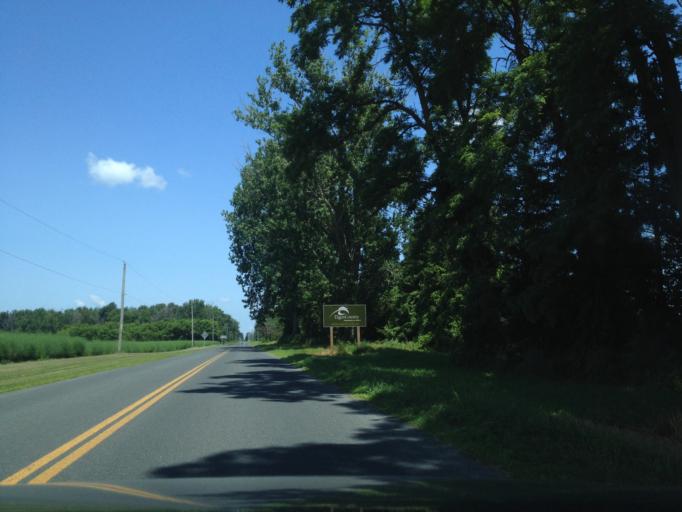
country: CA
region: Ontario
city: Aylmer
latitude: 42.6234
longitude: -80.7210
